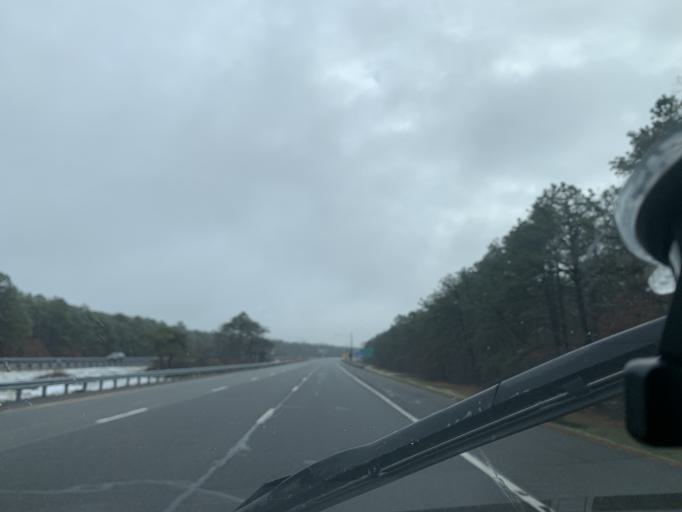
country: US
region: New Jersey
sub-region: Atlantic County
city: Pomona
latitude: 39.4380
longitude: -74.5962
